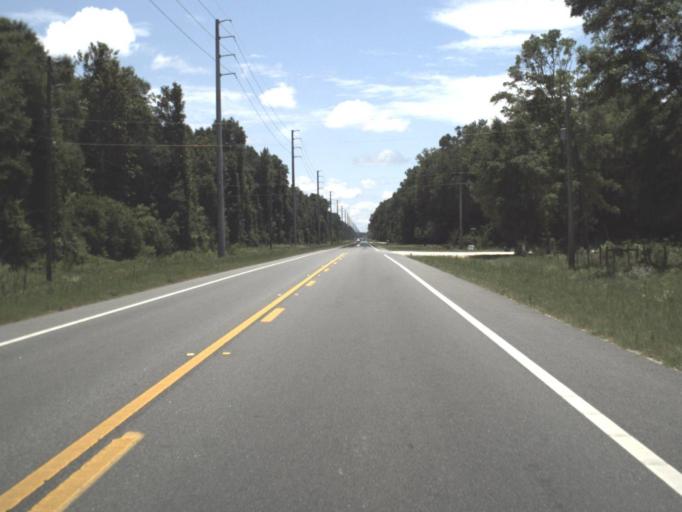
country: US
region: Florida
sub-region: Dixie County
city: Cross City
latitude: 29.6456
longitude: -82.9837
